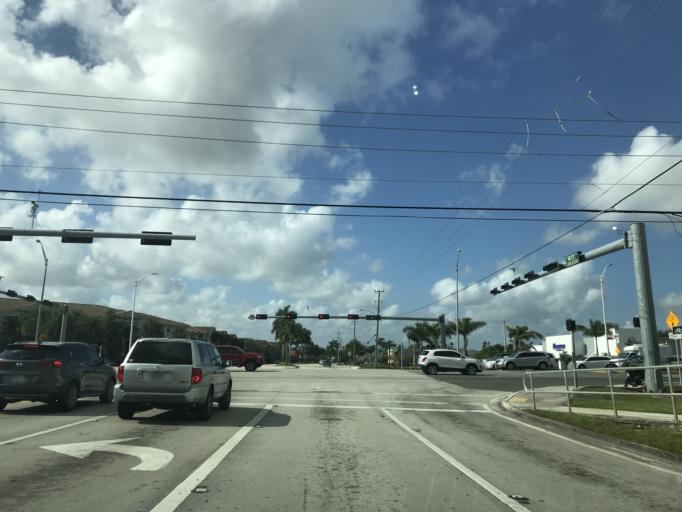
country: US
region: Florida
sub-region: Broward County
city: Margate
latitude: 26.2674
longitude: -80.2012
